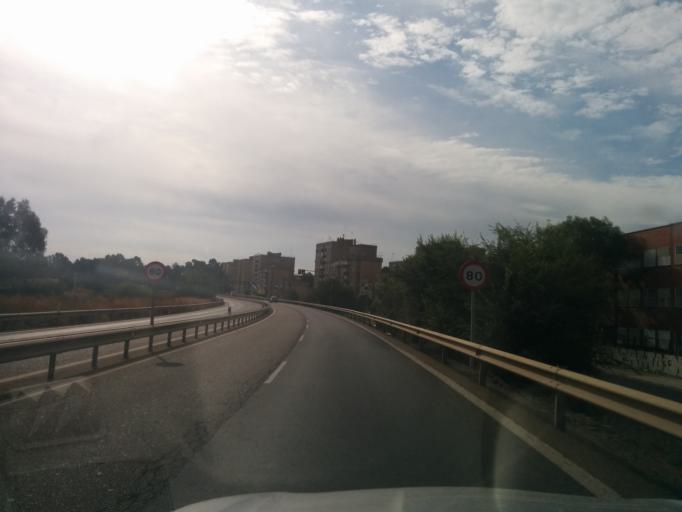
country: ES
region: Andalusia
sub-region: Provincia de Sevilla
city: Sevilla
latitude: 37.4260
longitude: -5.9630
